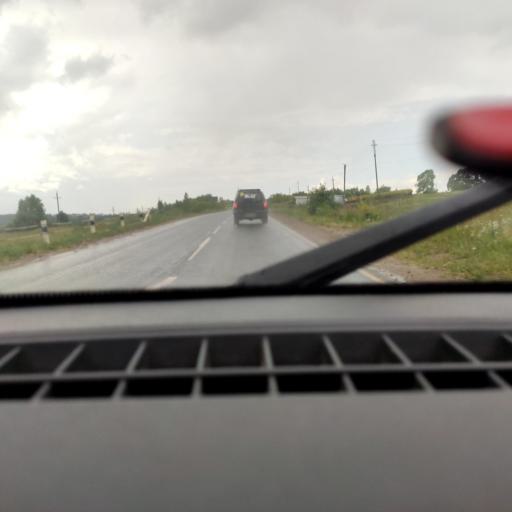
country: RU
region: Bashkortostan
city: Kabakovo
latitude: 54.5864
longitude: 56.2583
